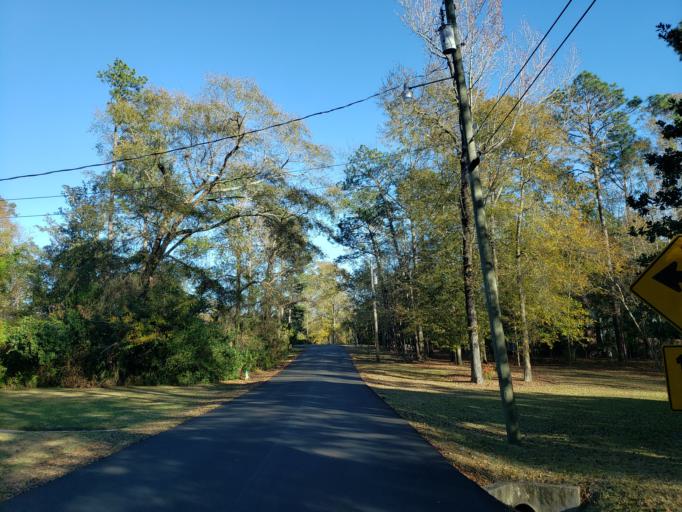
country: US
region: Mississippi
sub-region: Forrest County
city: Hattiesburg
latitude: 31.3137
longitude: -89.3175
